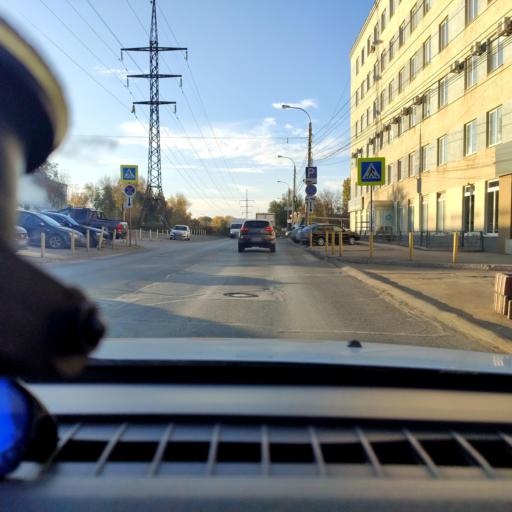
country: RU
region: Samara
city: Samara
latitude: 53.1905
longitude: 50.1720
